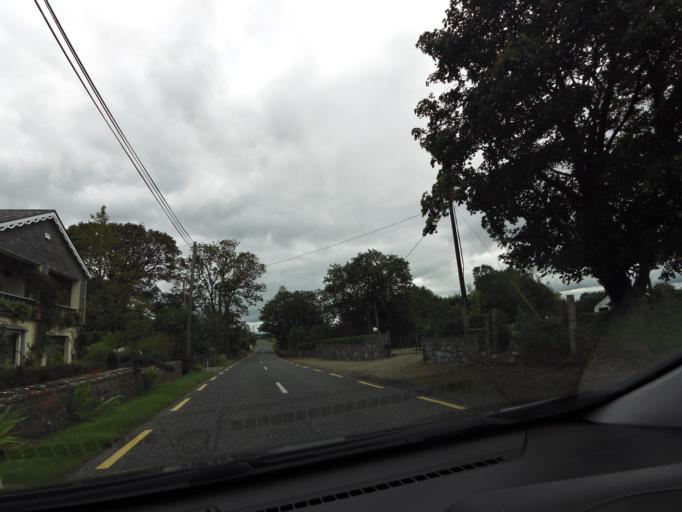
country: IE
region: Connaught
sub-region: County Galway
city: Ballinasloe
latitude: 53.3024
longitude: -8.1321
